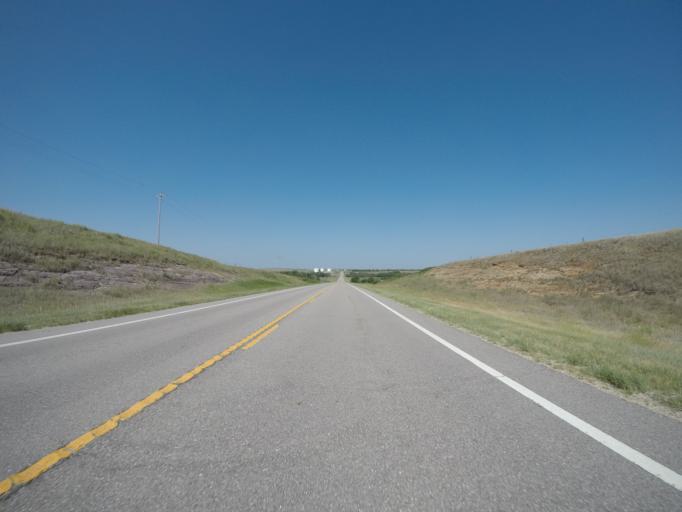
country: US
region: Kansas
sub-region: Cloud County
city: Concordia
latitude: 39.3648
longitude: -97.6141
